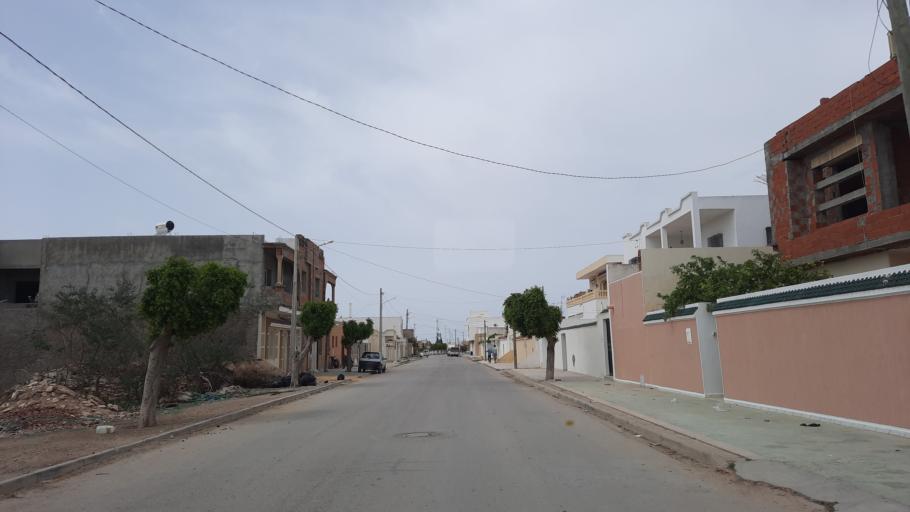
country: TN
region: Al Mahdiyah
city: El Jem
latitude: 35.3001
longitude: 10.7055
